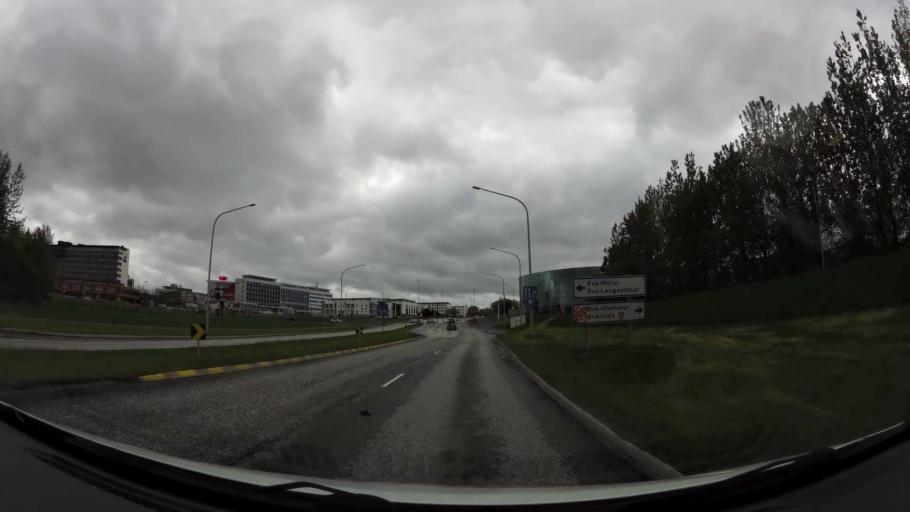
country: IS
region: Capital Region
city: Reykjavik
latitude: 64.1413
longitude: -21.8931
